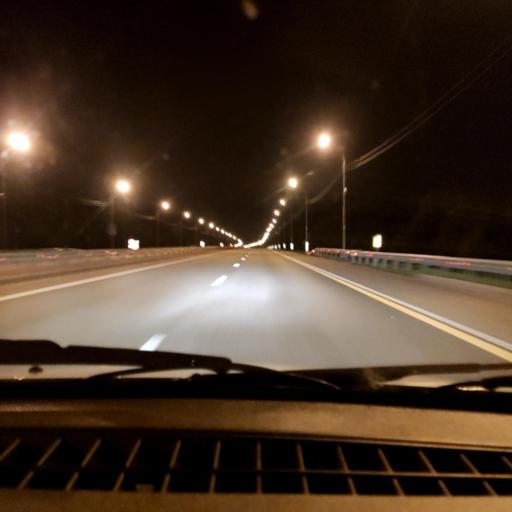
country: RU
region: Lipetsk
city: Zadonsk
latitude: 52.3492
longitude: 38.9501
